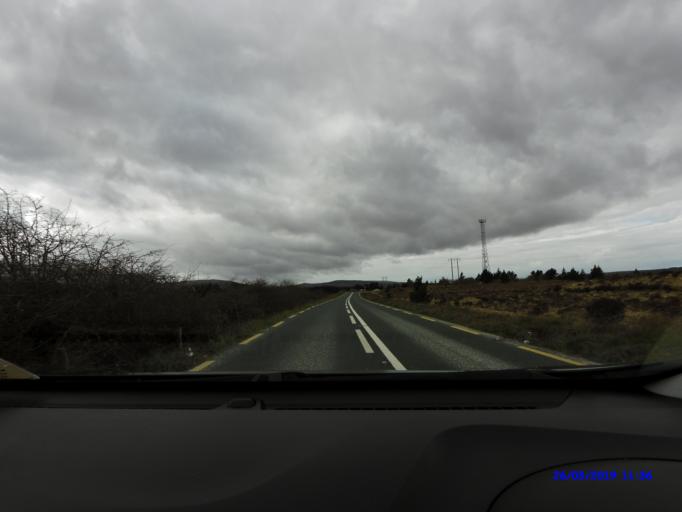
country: IE
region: Connaught
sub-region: Maigh Eo
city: Crossmolina
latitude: 54.1221
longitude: -9.5936
